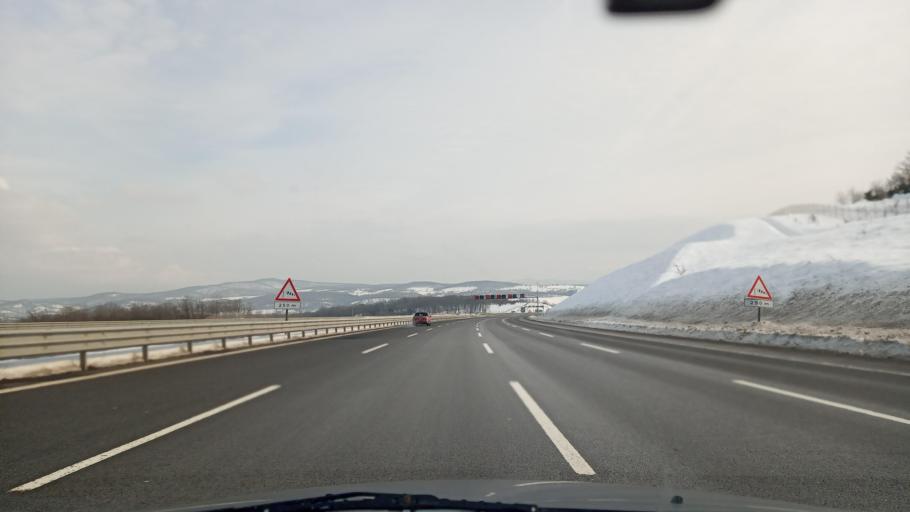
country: TR
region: Kocaeli
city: Mollafeneri
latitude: 40.9190
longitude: 29.4974
